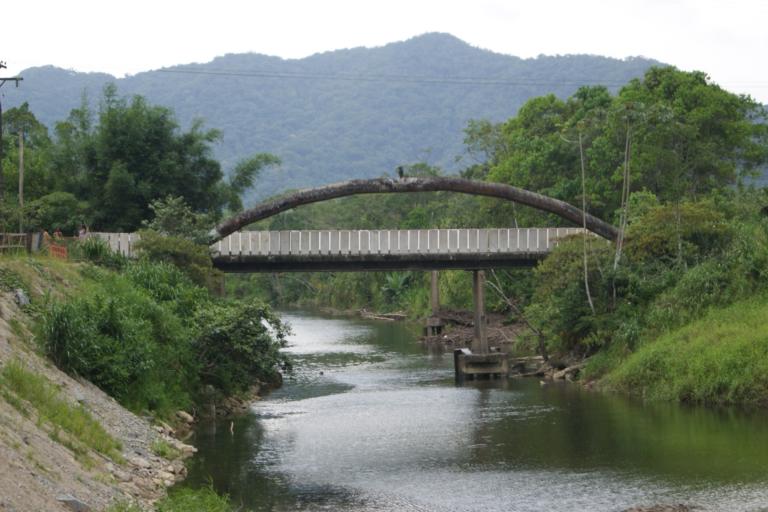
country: BR
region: Sao Paulo
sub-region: Itanhaem
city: Itanhaem
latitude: -24.0823
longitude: -46.8021
